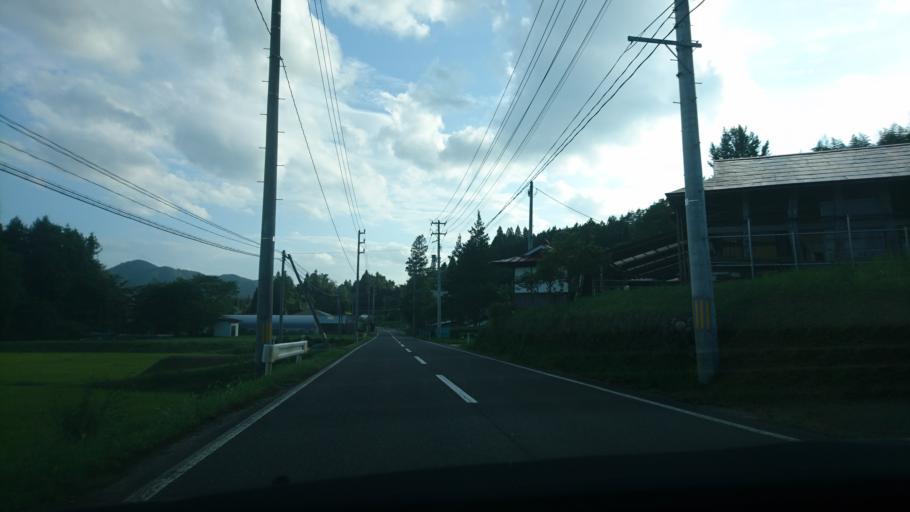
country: JP
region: Iwate
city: Ichinoseki
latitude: 39.0024
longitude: 141.2823
